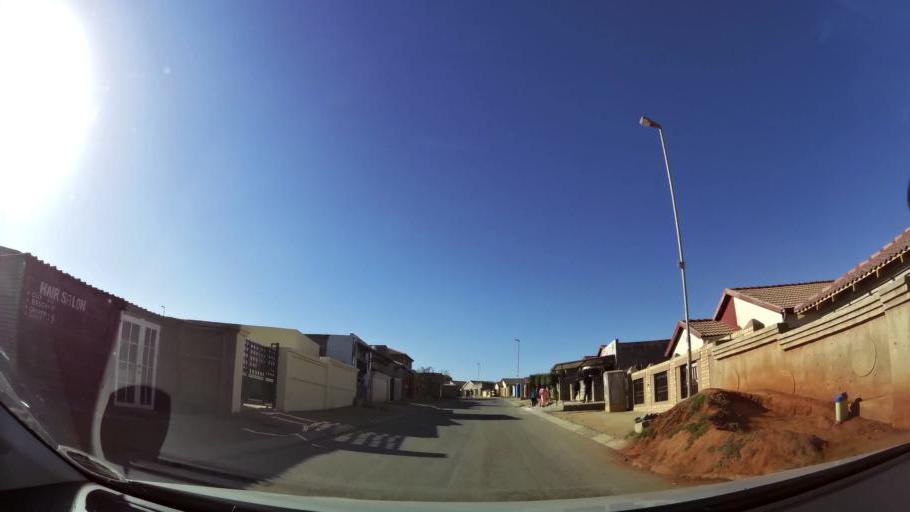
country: ZA
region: Gauteng
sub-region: Ekurhuleni Metropolitan Municipality
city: Tembisa
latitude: -26.0306
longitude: 28.2145
